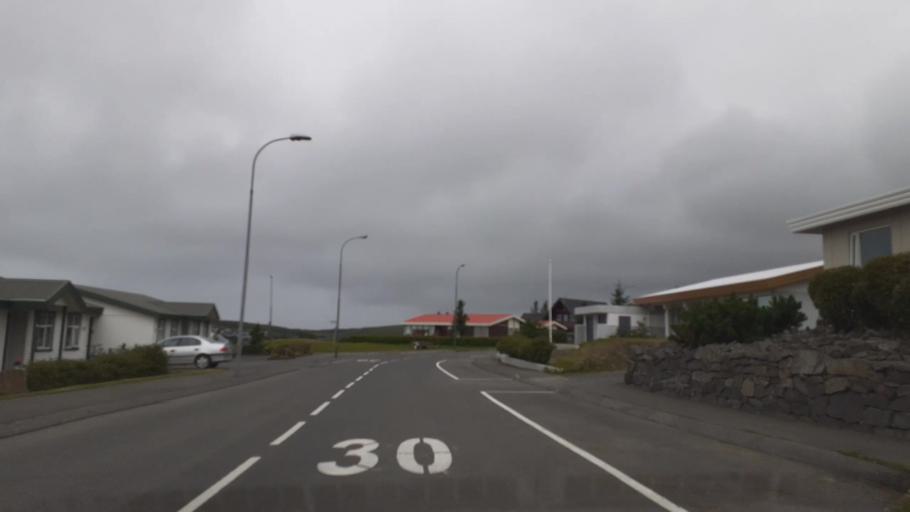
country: IS
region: Northeast
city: Husavik
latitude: 66.0374
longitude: -17.3365
